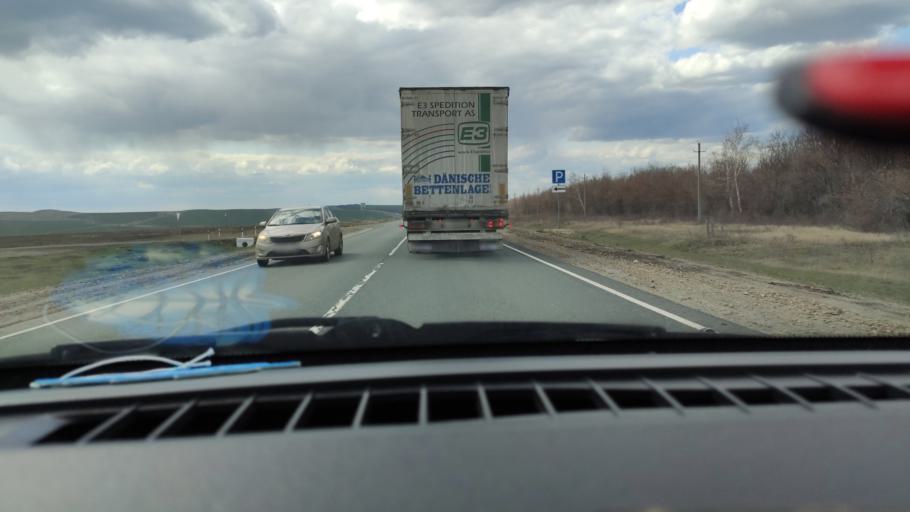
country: RU
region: Saratov
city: Alekseyevka
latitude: 52.2616
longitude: 47.9214
